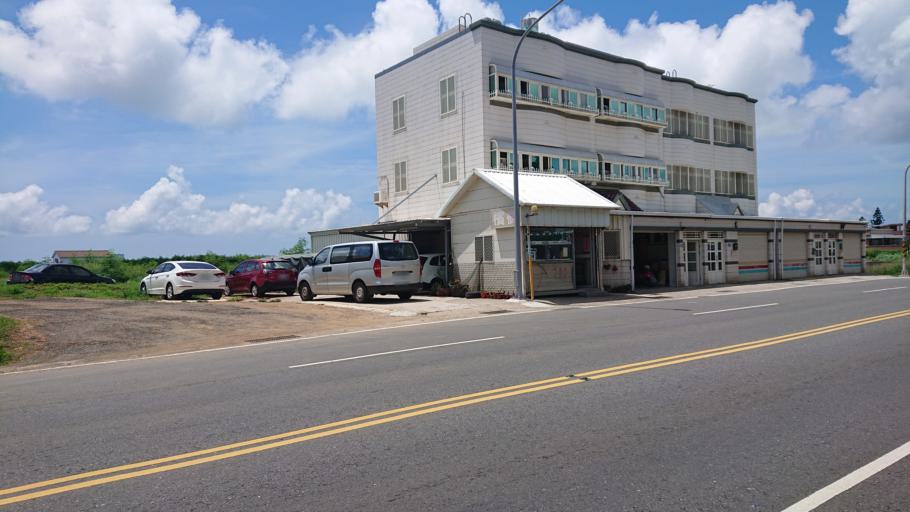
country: TW
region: Taiwan
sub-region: Penghu
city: Ma-kung
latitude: 23.5721
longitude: 119.5998
